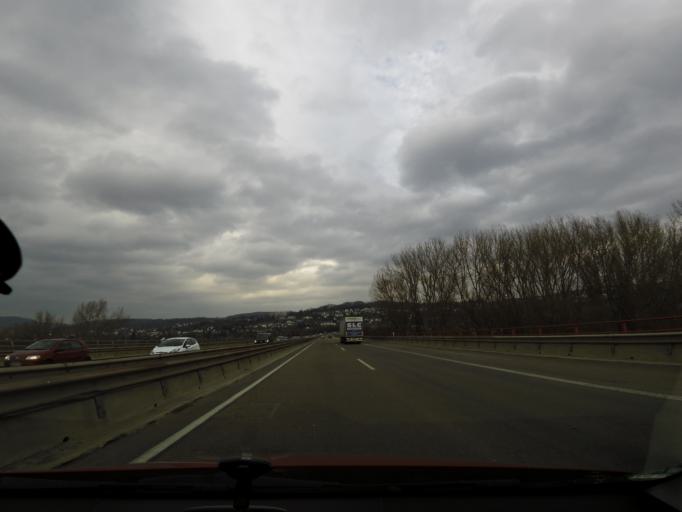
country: DE
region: Rheinland-Pfalz
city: Sankt Sebastian
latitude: 50.4098
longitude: 7.5741
